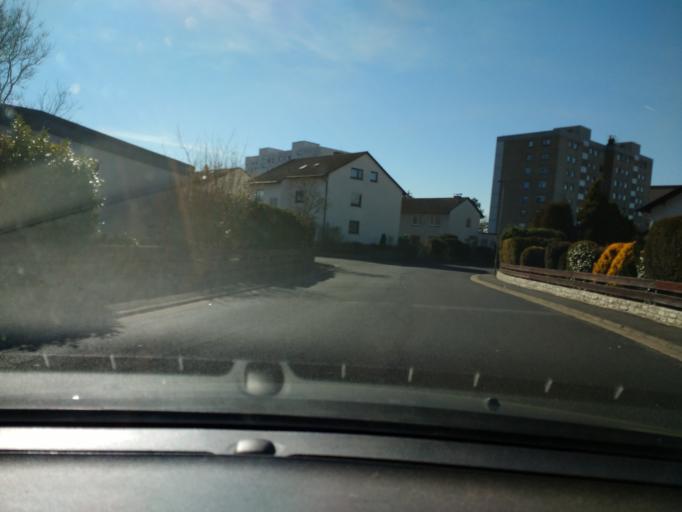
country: DE
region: Hesse
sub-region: Regierungsbezirk Darmstadt
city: Rodenbach
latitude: 50.1391
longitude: 9.0314
